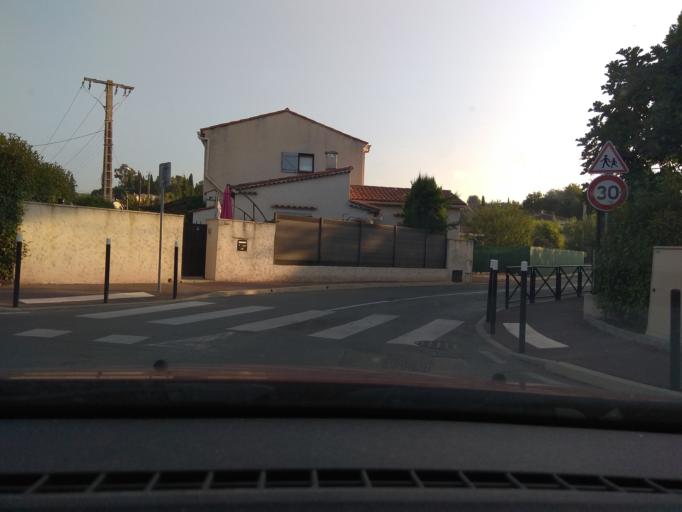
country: FR
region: Provence-Alpes-Cote d'Azur
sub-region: Departement des Alpes-Maritimes
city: Villeneuve-Loubet
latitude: 43.6751
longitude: 7.1094
